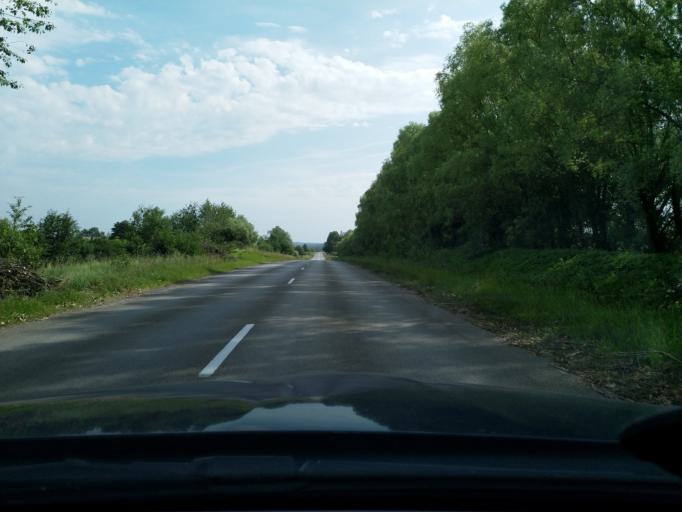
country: LV
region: Tukuma Rajons
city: Tukums
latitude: 56.9304
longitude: 23.0824
